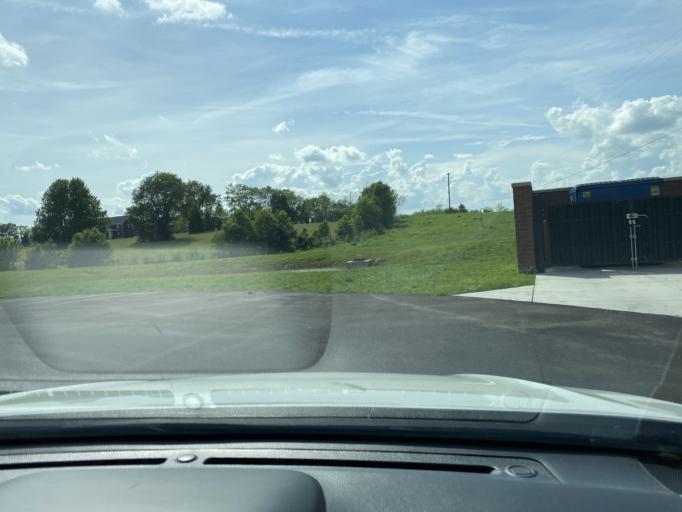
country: US
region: Kentucky
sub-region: Scott County
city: Georgetown
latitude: 38.2144
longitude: -84.6029
